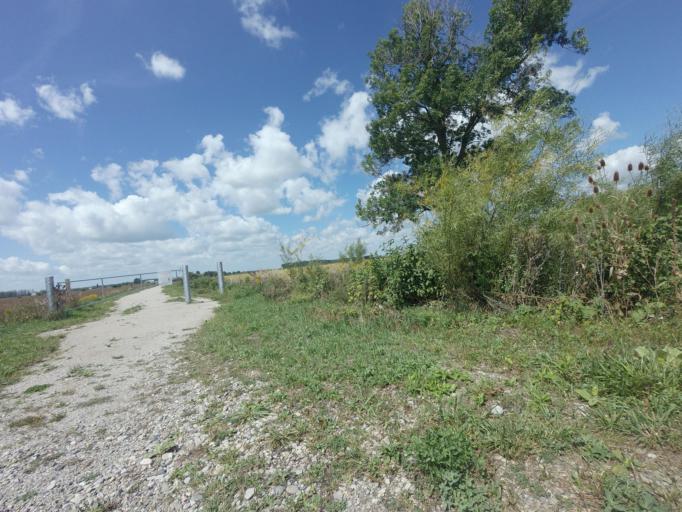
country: CA
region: Ontario
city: North Perth
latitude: 43.5630
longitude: -81.0143
